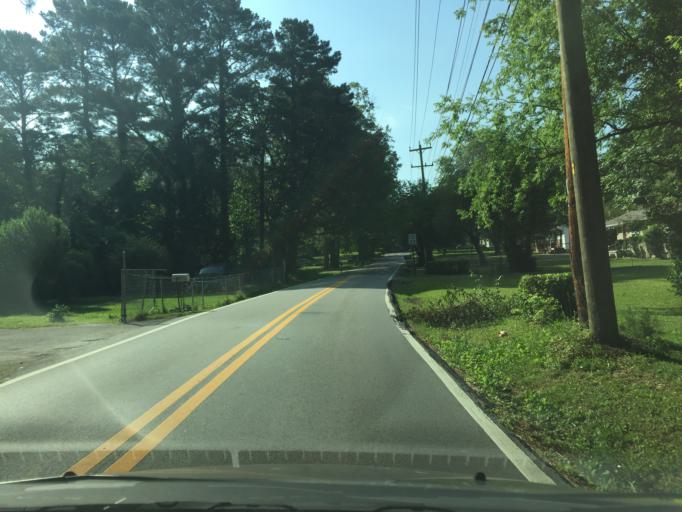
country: US
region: Tennessee
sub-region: Hamilton County
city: East Brainerd
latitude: 35.0356
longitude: -85.1886
